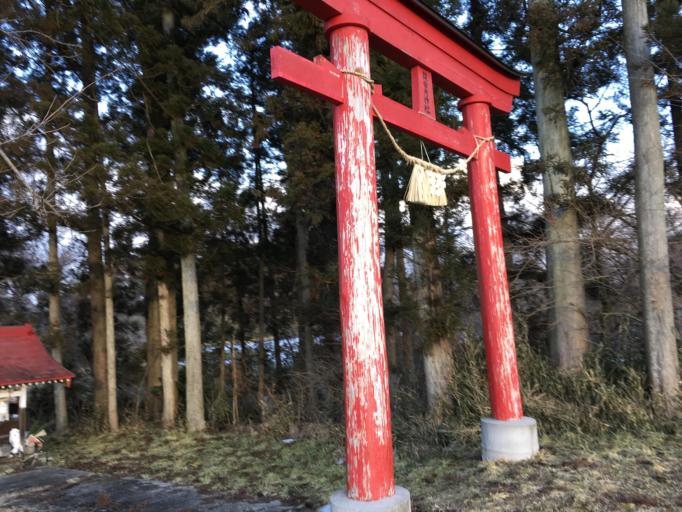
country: JP
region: Iwate
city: Ichinoseki
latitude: 38.8179
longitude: 141.0242
